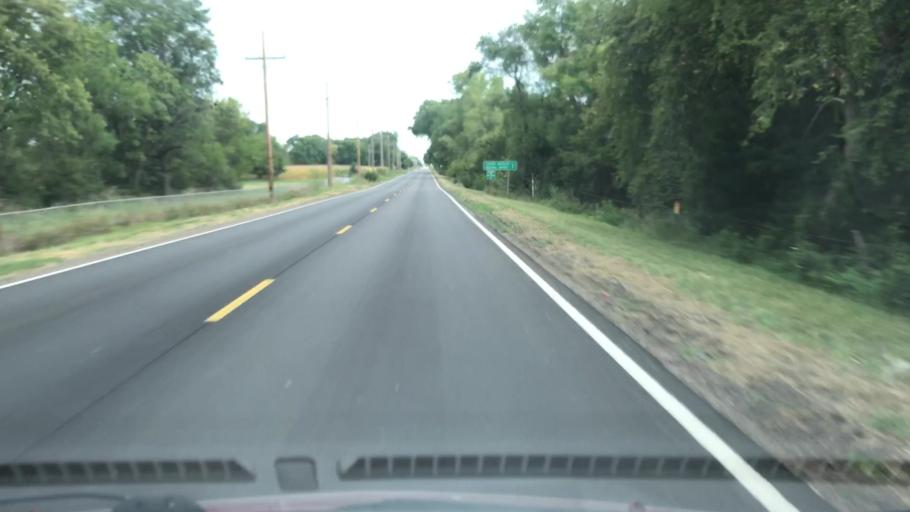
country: US
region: Nebraska
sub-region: Hall County
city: Grand Island
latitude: 40.9245
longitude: -98.3015
